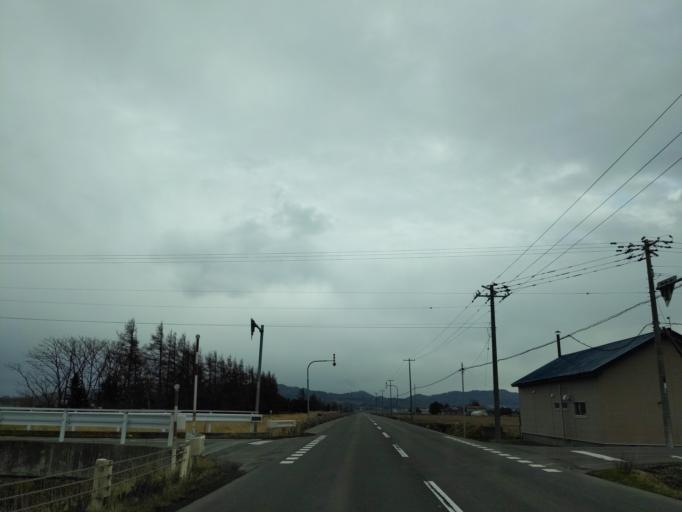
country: JP
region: Hokkaido
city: Kitahiroshima
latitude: 43.0399
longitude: 141.6895
